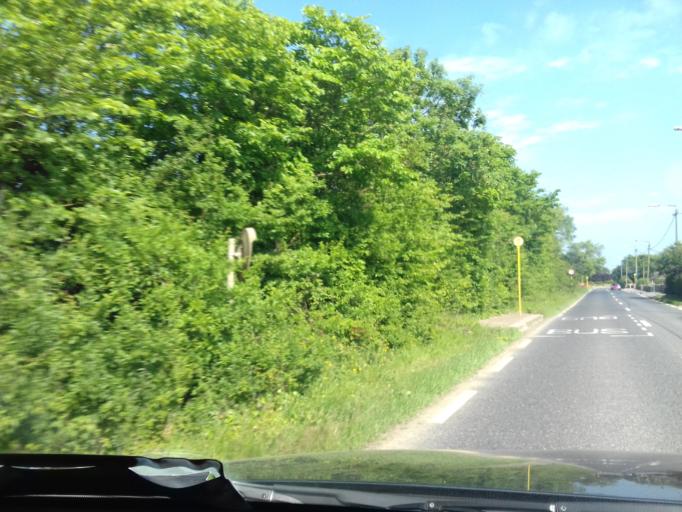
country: IE
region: Leinster
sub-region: Fingal County
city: Swords
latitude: 53.4726
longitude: -6.2539
